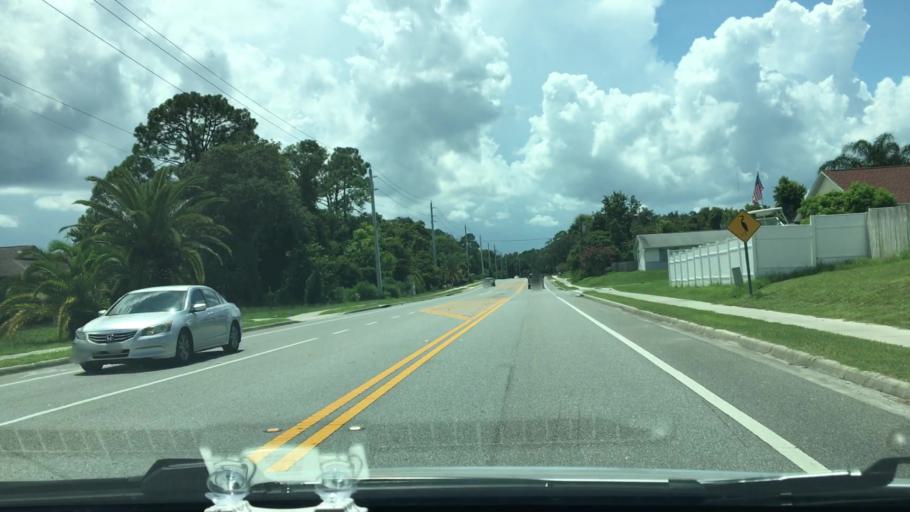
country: US
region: Florida
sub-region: Volusia County
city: Deltona
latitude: 28.8774
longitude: -81.1886
